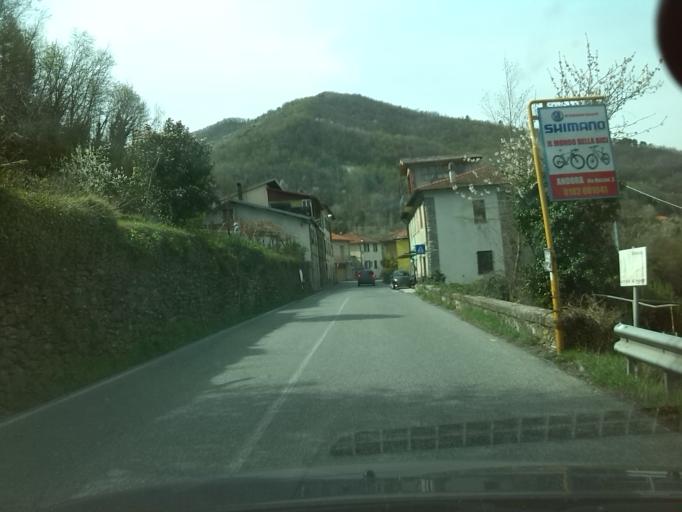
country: IT
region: Liguria
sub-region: Provincia di Imperia
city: Vessalico
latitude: 44.0389
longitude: 7.9454
